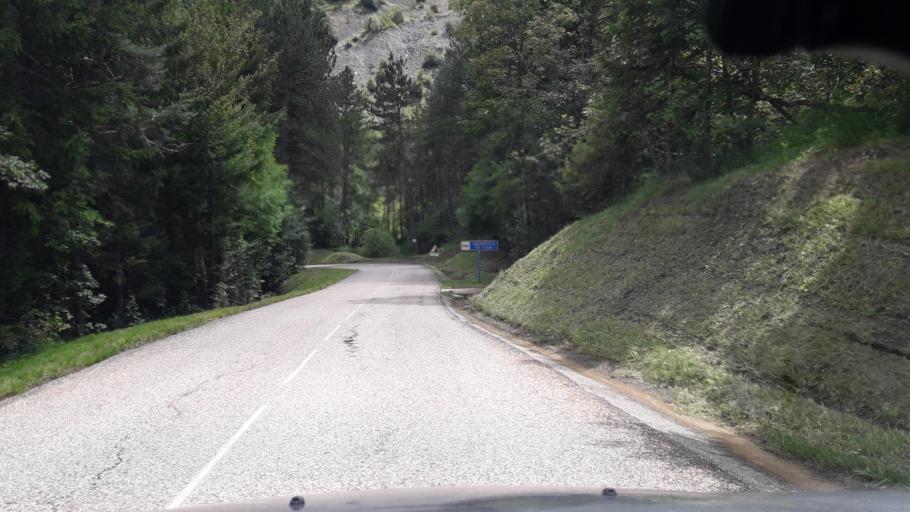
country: FR
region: Rhone-Alpes
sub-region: Departement de la Savoie
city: Saint-Baldoph
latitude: 45.4779
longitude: 5.9213
